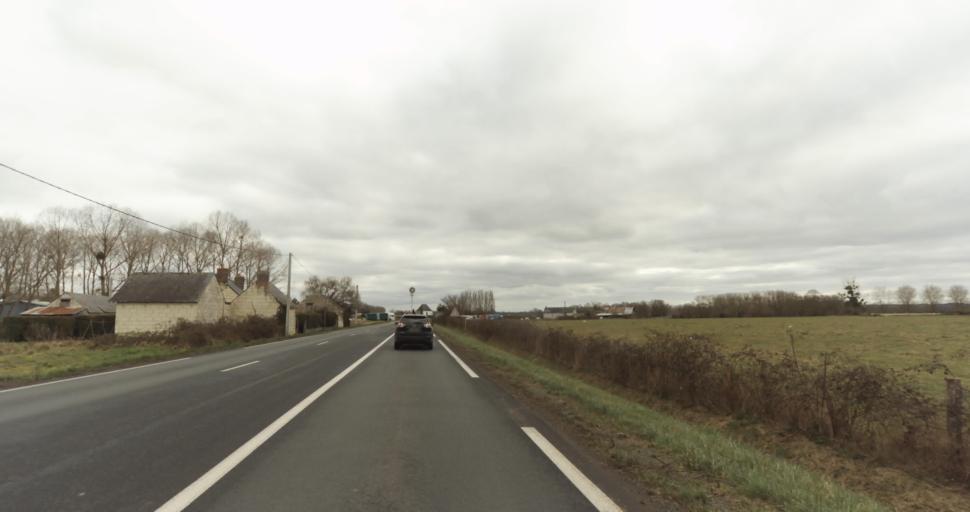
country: FR
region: Pays de la Loire
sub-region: Departement de Maine-et-Loire
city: Vivy
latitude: 47.3071
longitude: -0.0381
